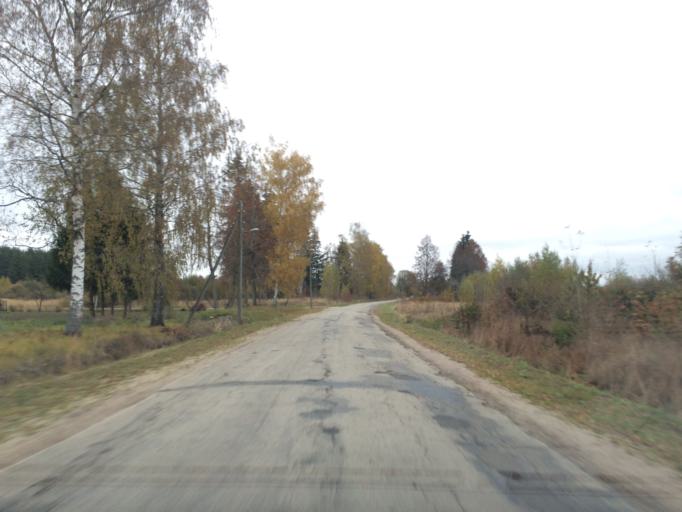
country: LV
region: Plavinu
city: Plavinas
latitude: 56.6162
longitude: 25.7639
